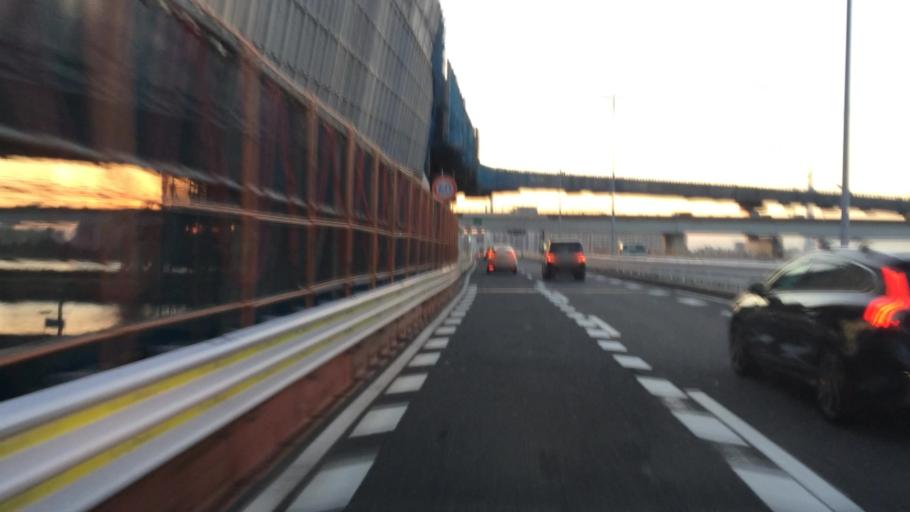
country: JP
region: Tokyo
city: Urayasu
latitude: 35.6990
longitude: 139.8622
